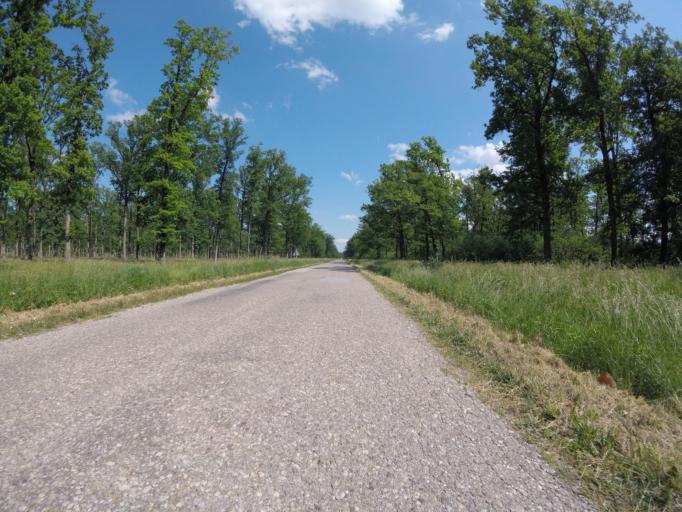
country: HR
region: Zagrebacka
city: Kuce
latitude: 45.6786
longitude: 16.1600
